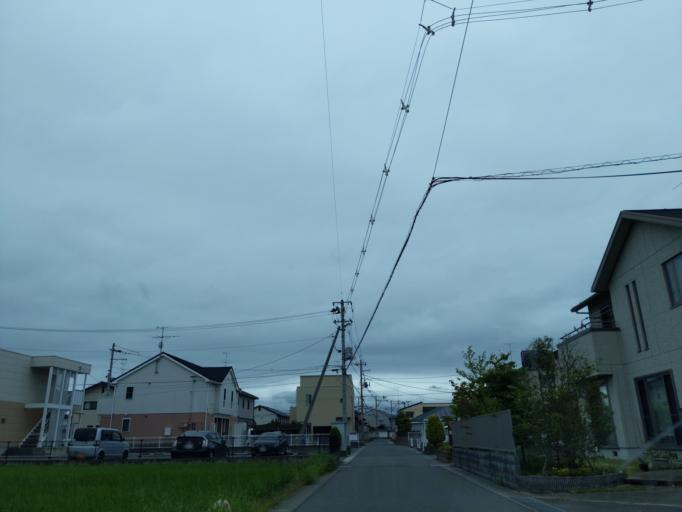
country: JP
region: Fukushima
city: Koriyama
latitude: 37.3709
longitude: 140.3671
